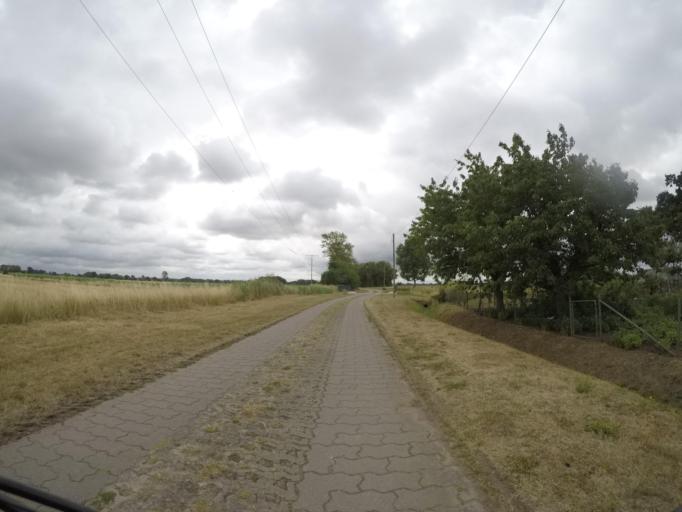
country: DE
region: Lower Saxony
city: Hitzacker
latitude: 53.1813
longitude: 11.1096
